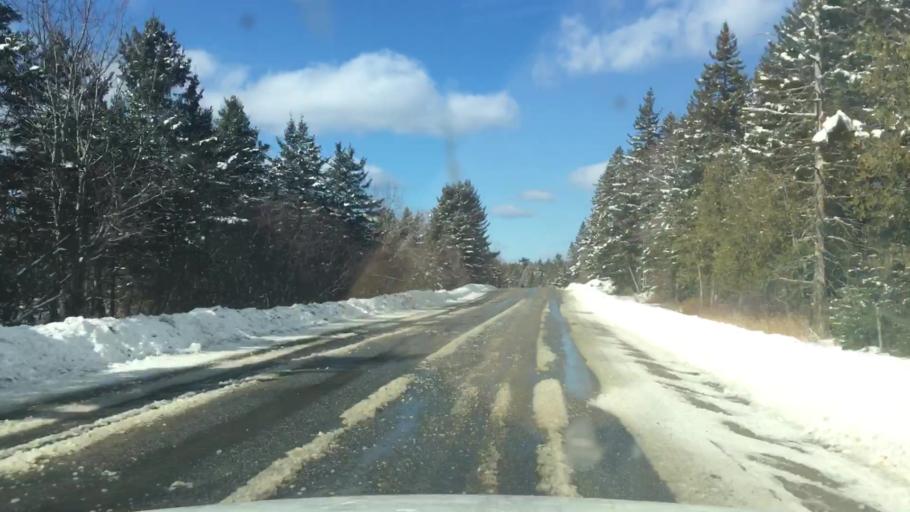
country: US
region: Maine
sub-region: Washington County
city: Machias
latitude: 44.6813
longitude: -67.4558
